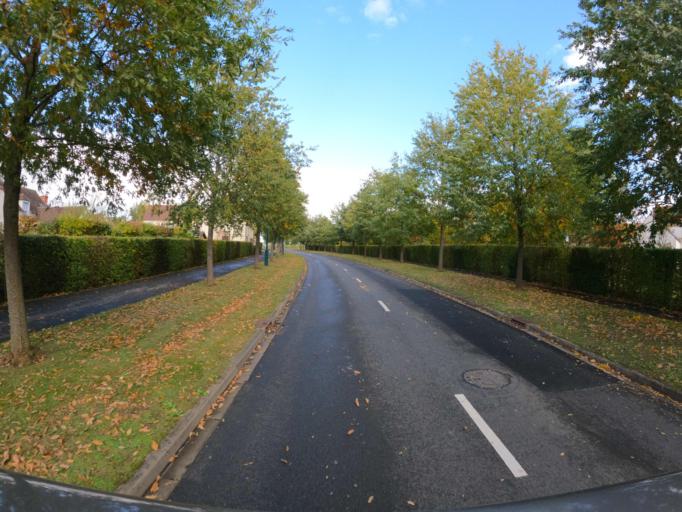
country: FR
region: Ile-de-France
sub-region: Departement de Seine-et-Marne
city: Magny-le-Hongre
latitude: 48.8779
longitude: 2.8131
